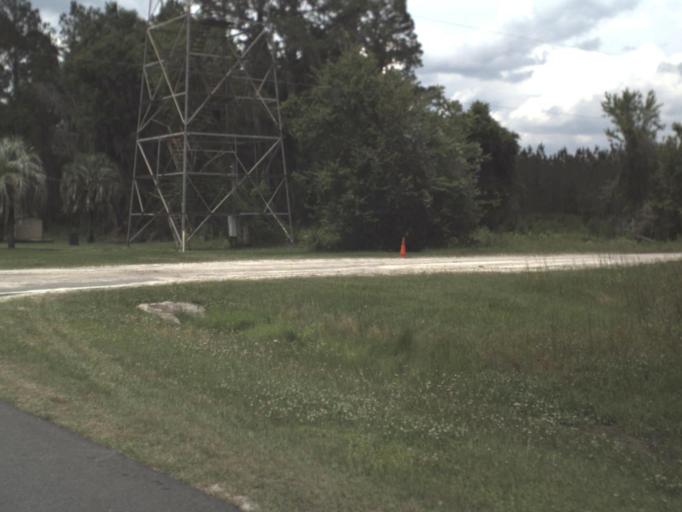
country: US
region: Florida
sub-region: Columbia County
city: Five Points
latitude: 30.4862
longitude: -82.6607
